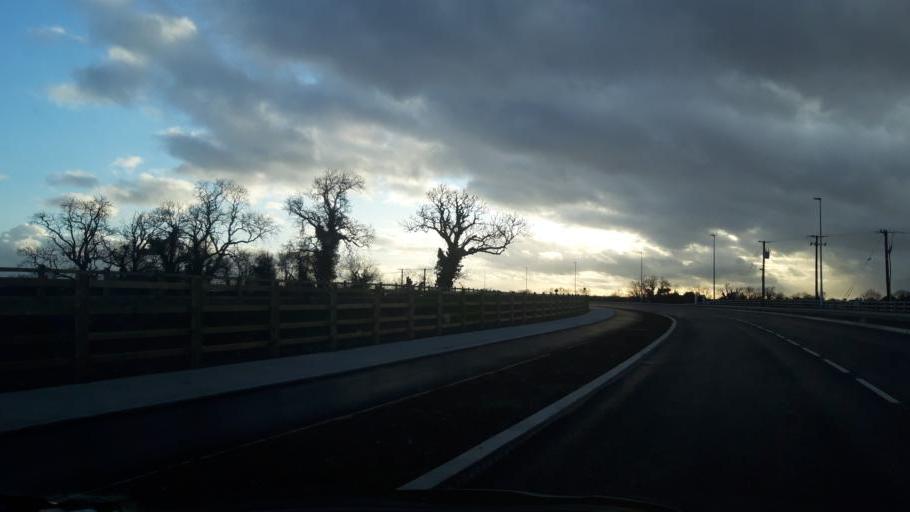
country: IE
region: Leinster
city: Donabate
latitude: 53.4888
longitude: -6.1333
